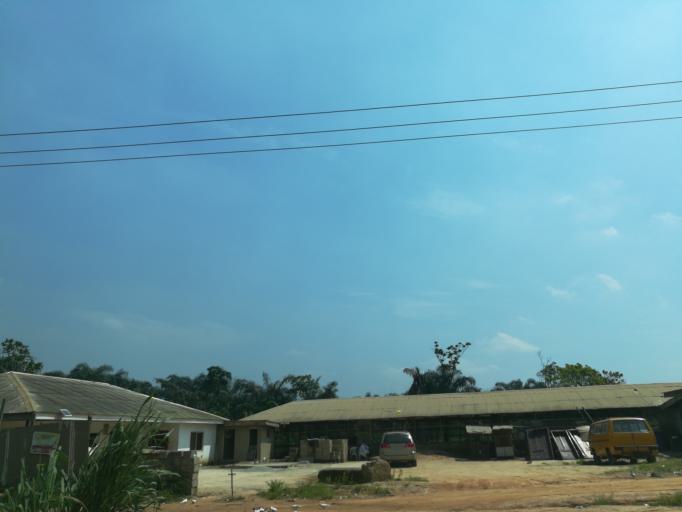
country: NG
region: Lagos
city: Ikorodu
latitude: 6.6623
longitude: 3.4688
